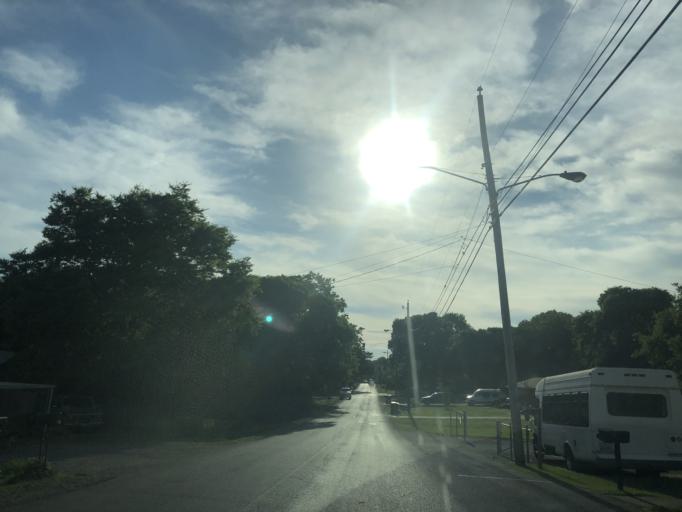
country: US
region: Tennessee
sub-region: Davidson County
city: Nashville
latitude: 36.2113
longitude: -86.8407
